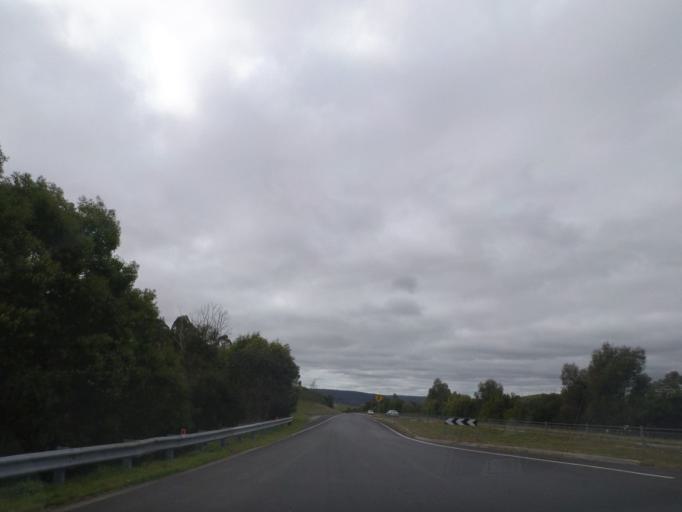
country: AU
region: Victoria
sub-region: Whittlesea
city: Whittlesea
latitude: -37.3211
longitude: 145.0372
